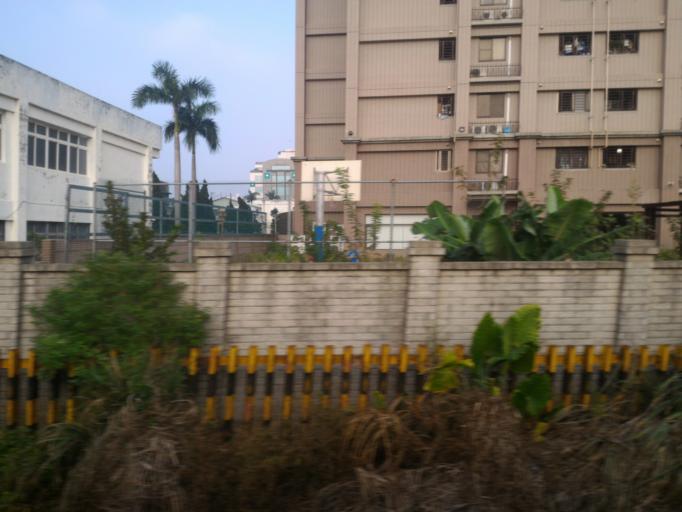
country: TW
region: Taiwan
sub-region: Taoyuan
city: Taoyuan
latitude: 24.9872
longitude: 121.3236
